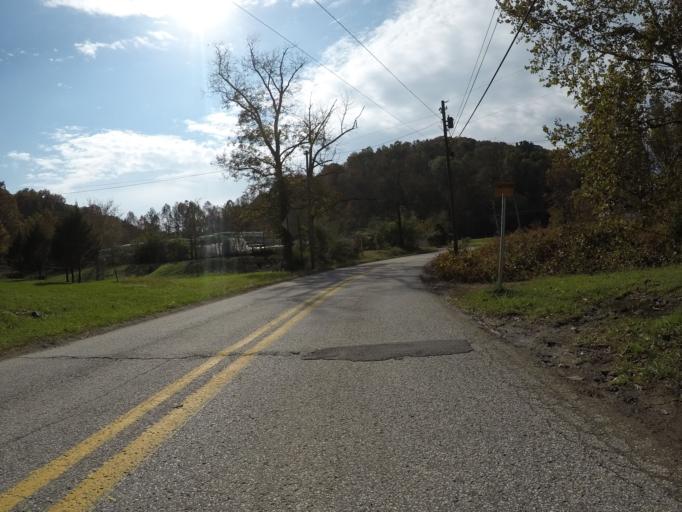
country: US
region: West Virginia
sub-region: Cabell County
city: Huntington
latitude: 38.3818
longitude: -82.3956
